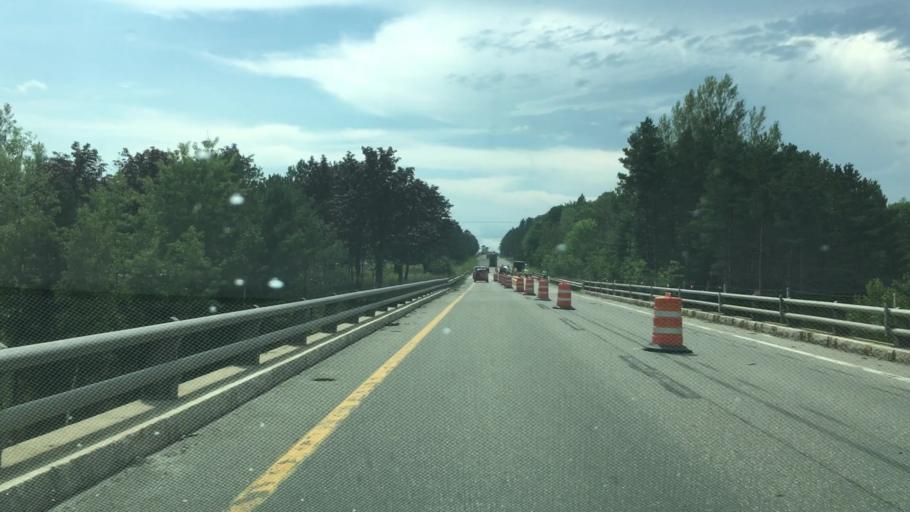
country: US
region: Maine
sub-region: Penobscot County
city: Medway
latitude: 45.6019
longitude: -68.5295
